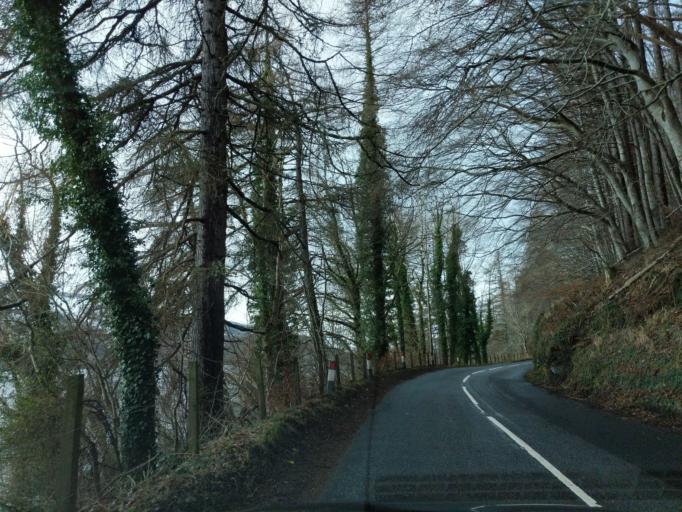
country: GB
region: Scotland
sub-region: Perth and Kinross
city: Aberfeldy
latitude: 56.5774
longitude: -4.0402
